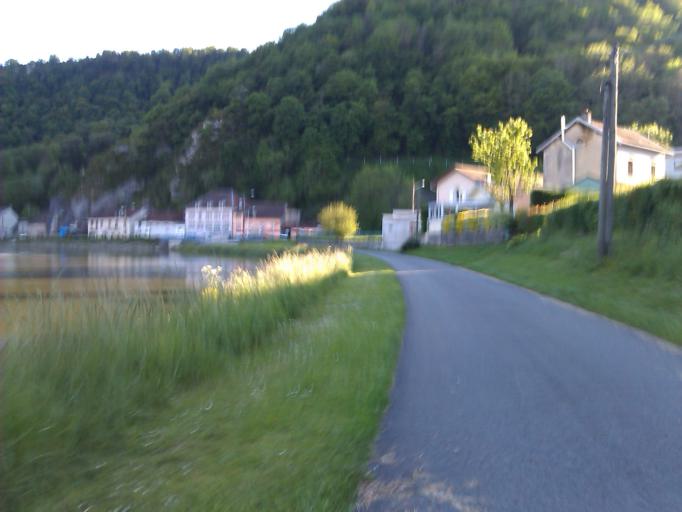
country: FR
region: Franche-Comte
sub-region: Departement du Doubs
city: Clerval
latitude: 47.3948
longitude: 6.4945
